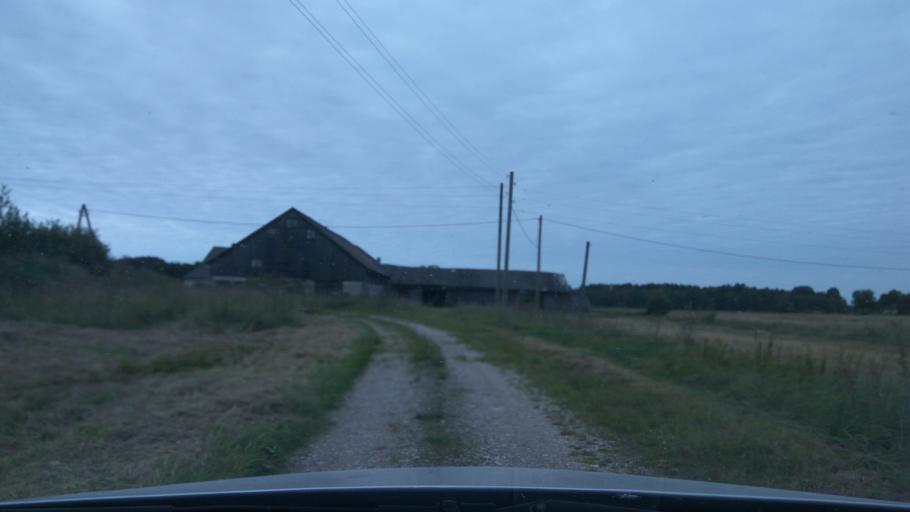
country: LV
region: Kuldigas Rajons
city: Kuldiga
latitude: 57.2440
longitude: 21.9458
